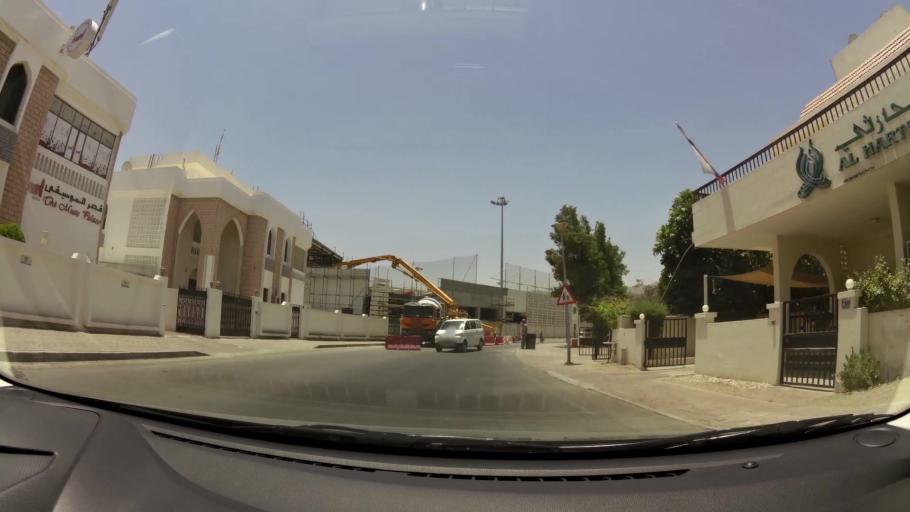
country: OM
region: Muhafazat Masqat
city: Bawshar
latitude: 23.6071
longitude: 58.4582
